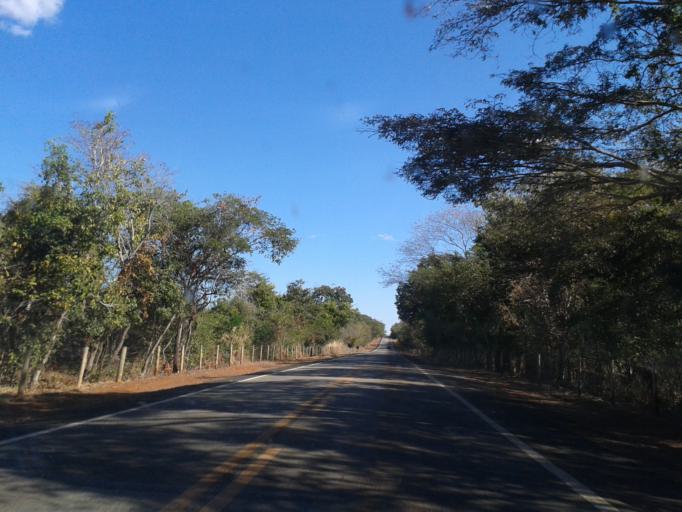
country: BR
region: Goias
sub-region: Mozarlandia
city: Mozarlandia
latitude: -14.6710
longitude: -50.5345
